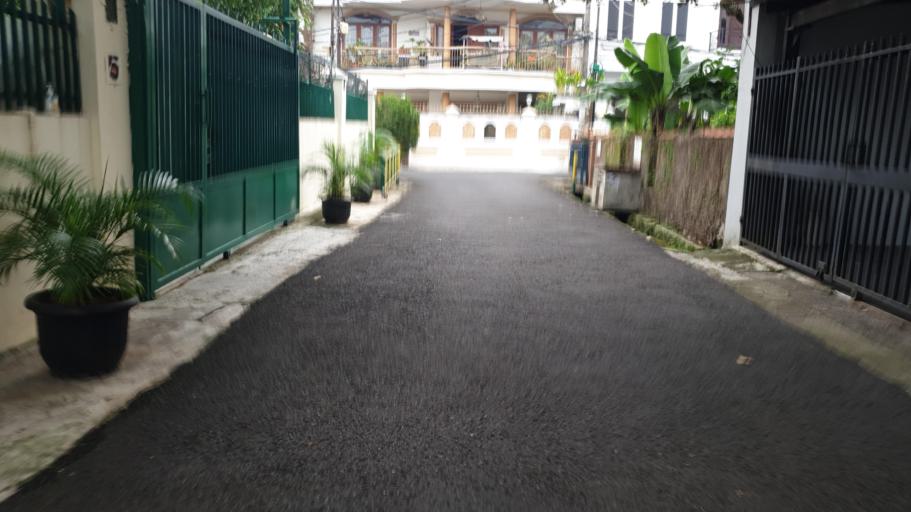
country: ID
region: Jakarta Raya
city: Jakarta
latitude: -6.2610
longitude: 106.7873
